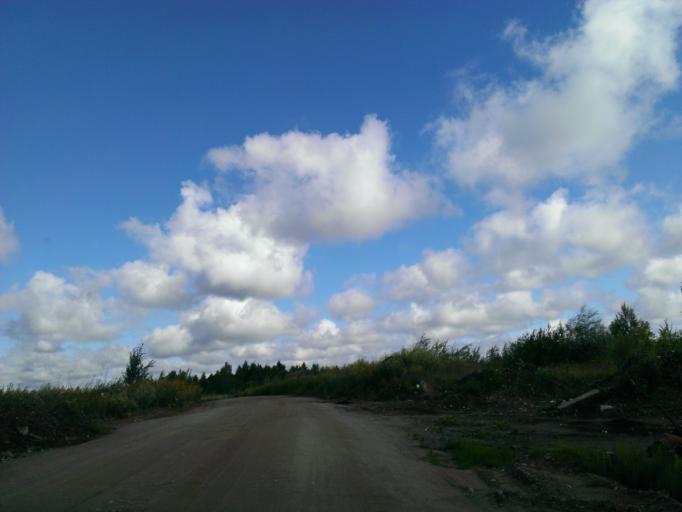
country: LV
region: Incukalns
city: Vangazi
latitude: 57.0898
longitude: 24.5137
